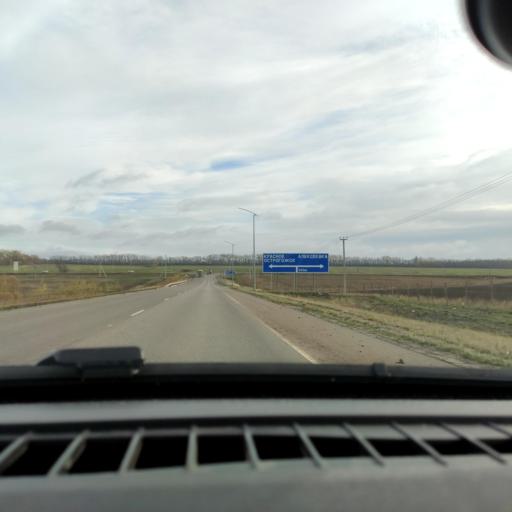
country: RU
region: Belgorod
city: Ilovka
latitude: 50.6858
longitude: 38.6557
